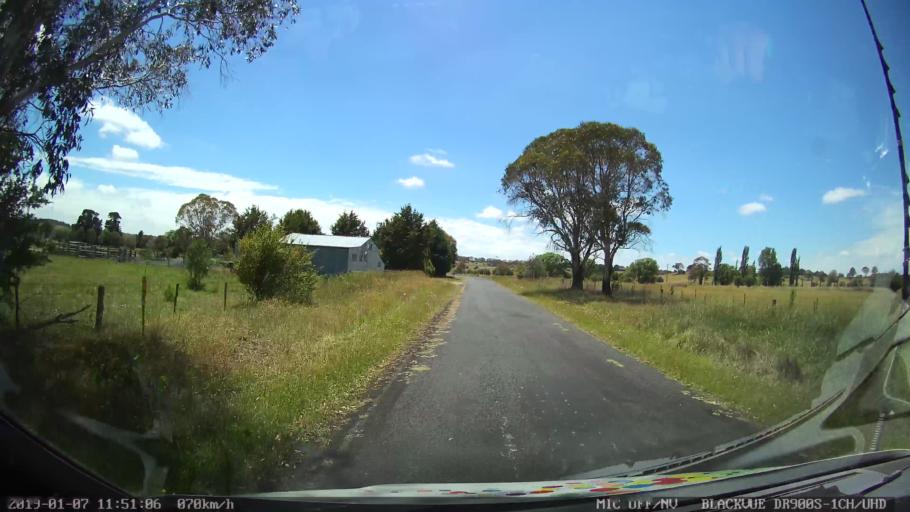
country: AU
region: New South Wales
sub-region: Guyra
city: Guyra
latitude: -30.3092
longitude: 151.6427
